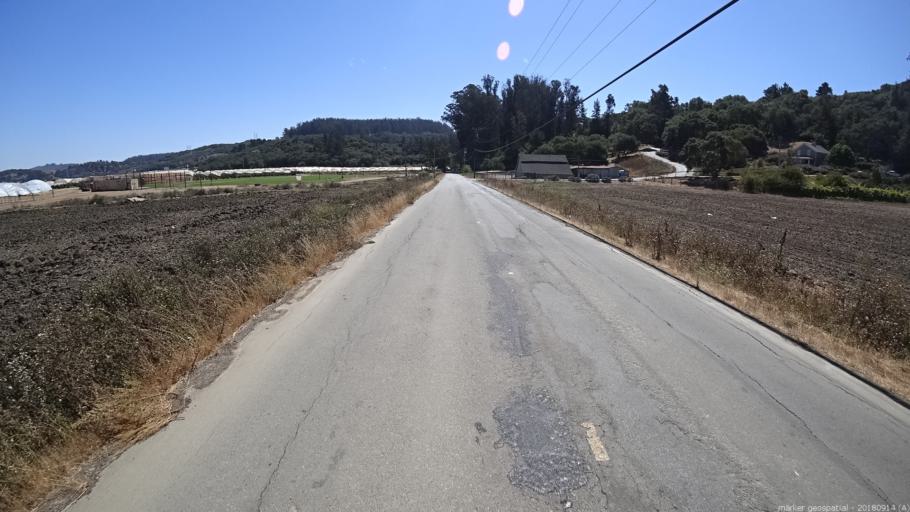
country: US
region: California
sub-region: San Benito County
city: Aromas
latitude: 36.8857
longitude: -121.6836
